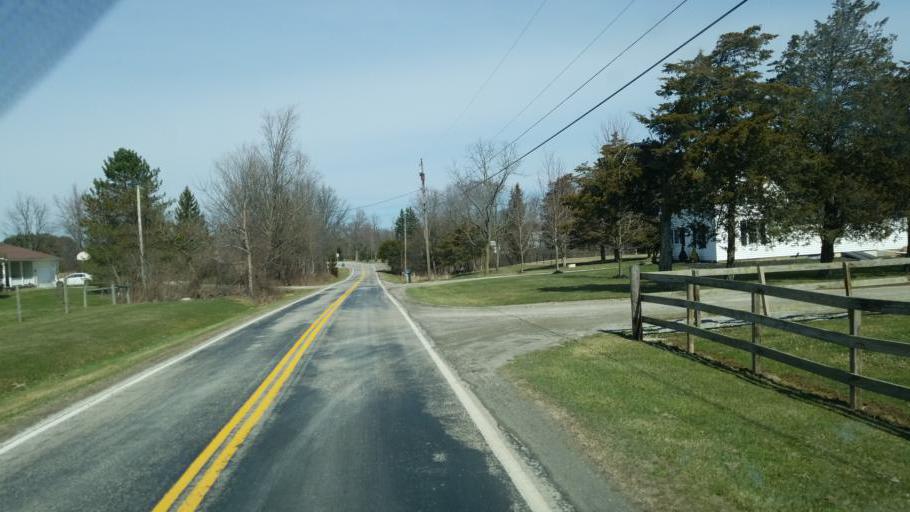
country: US
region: Ohio
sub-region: Lorain County
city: South Amherst
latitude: 41.3426
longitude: -82.2885
